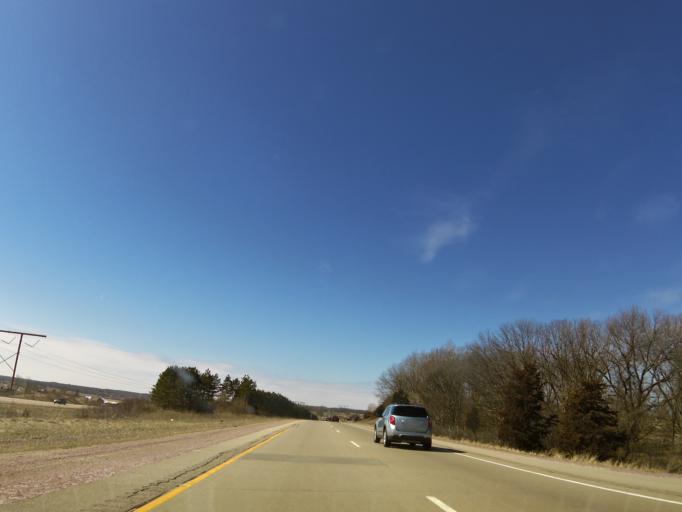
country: US
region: Wisconsin
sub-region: Sauk County
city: Baraboo
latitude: 43.5493
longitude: -89.6719
